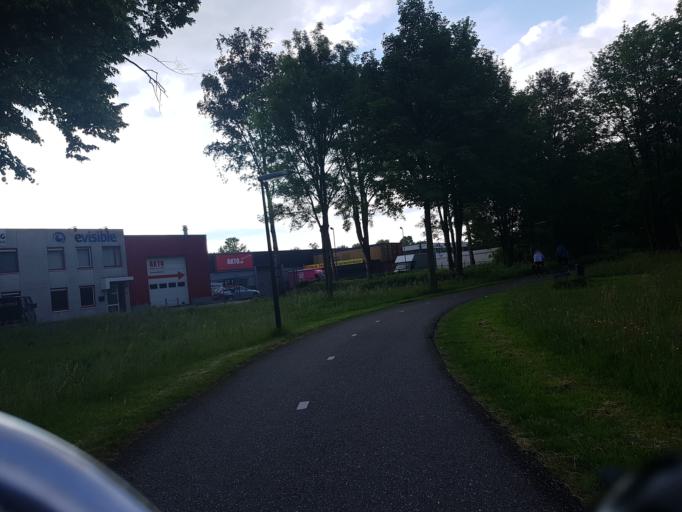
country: NL
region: Gelderland
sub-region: Gemeente Apeldoorn
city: Apeldoorn
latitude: 52.1883
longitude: 5.9877
